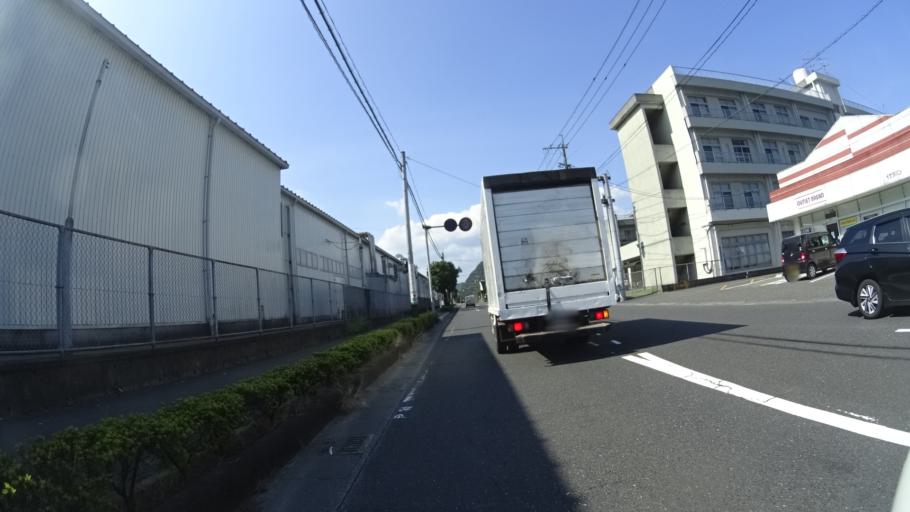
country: JP
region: Kagoshima
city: Kajiki
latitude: 31.7123
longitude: 130.6009
